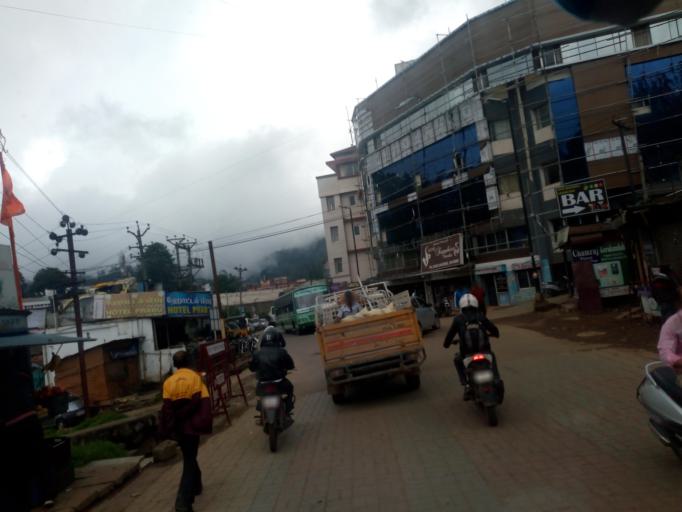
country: IN
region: Tamil Nadu
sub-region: Nilgiri
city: Ooty
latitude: 11.4097
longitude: 76.7087
